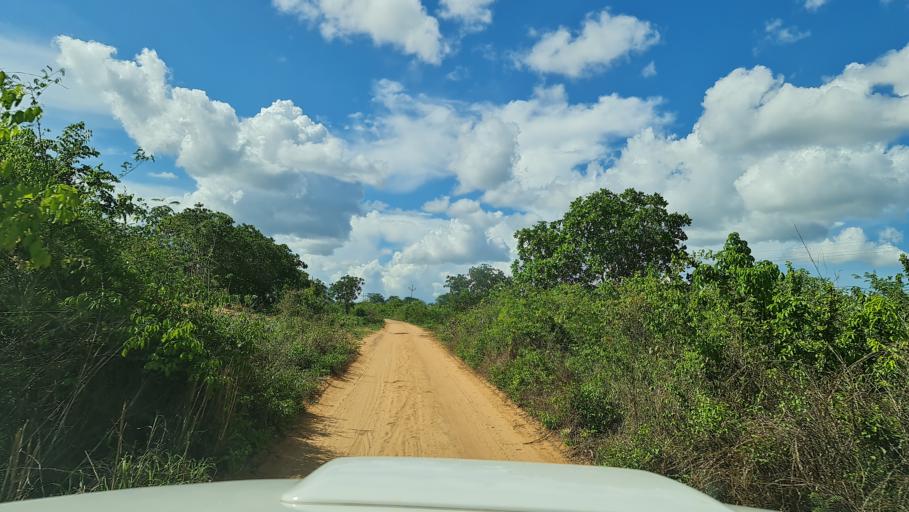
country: MZ
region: Nampula
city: Ilha de Mocambique
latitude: -15.4322
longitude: 40.2749
